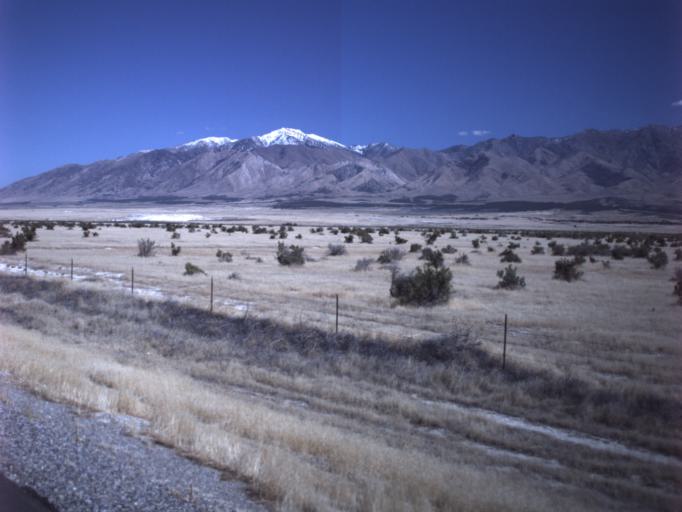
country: US
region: Utah
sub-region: Tooele County
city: Grantsville
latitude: 40.3145
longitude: -112.7435
